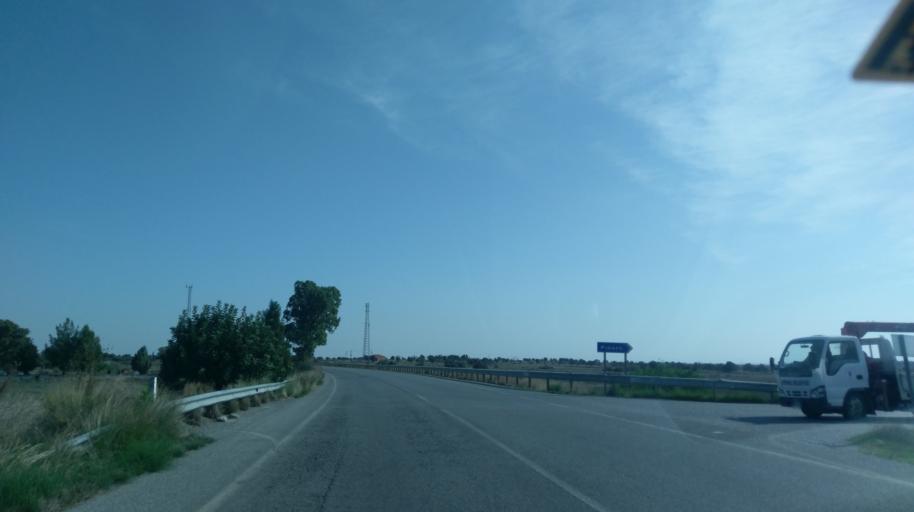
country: CY
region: Ammochostos
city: Lefkonoiko
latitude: 35.2597
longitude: 33.6575
